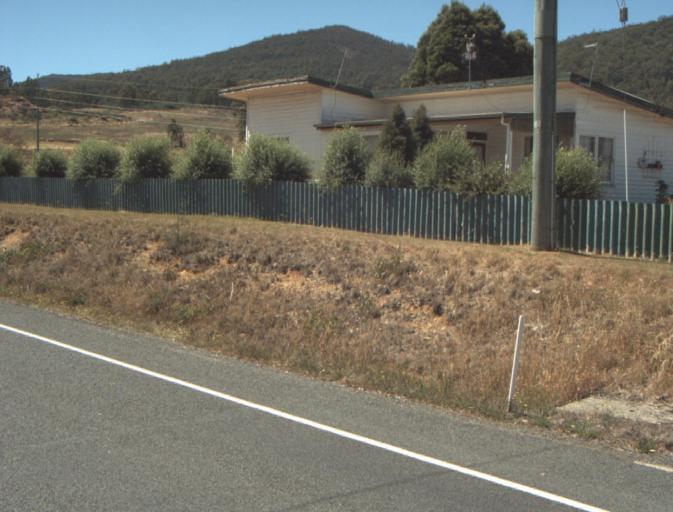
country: AU
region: Tasmania
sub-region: Launceston
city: Newstead
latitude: -41.3886
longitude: 147.3025
